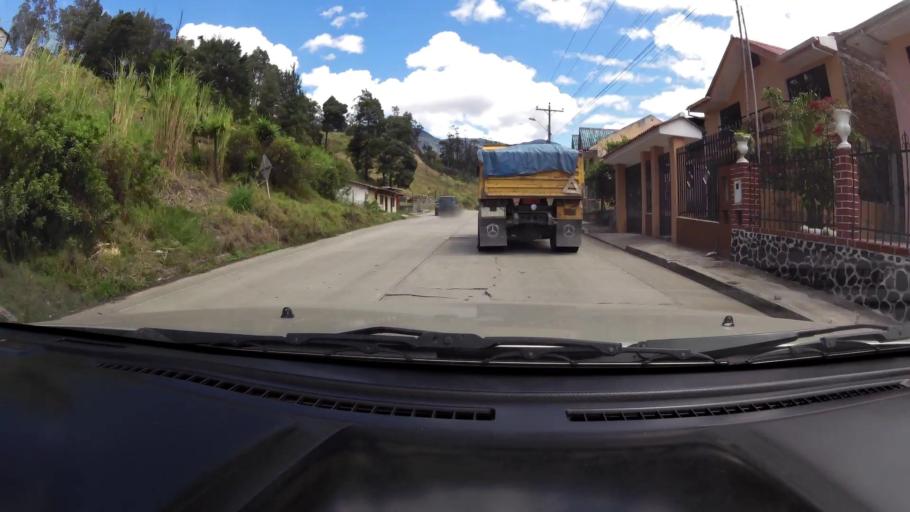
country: EC
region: Azuay
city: Cuenca
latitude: -3.1681
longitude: -79.1539
